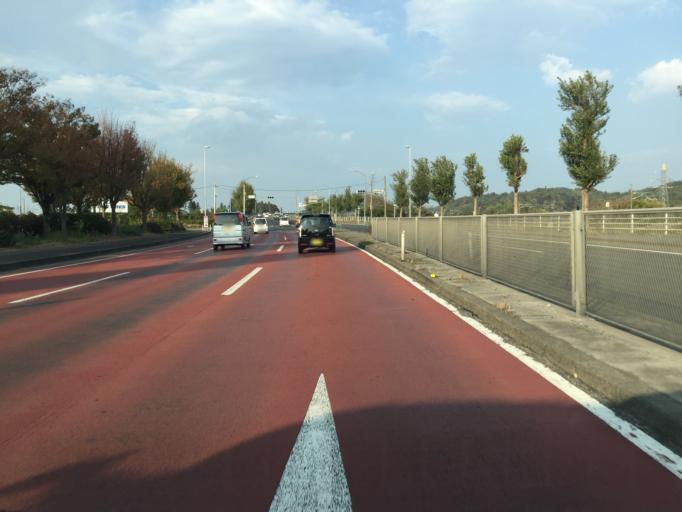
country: JP
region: Fukushima
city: Nihommatsu
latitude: 37.5989
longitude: 140.4614
